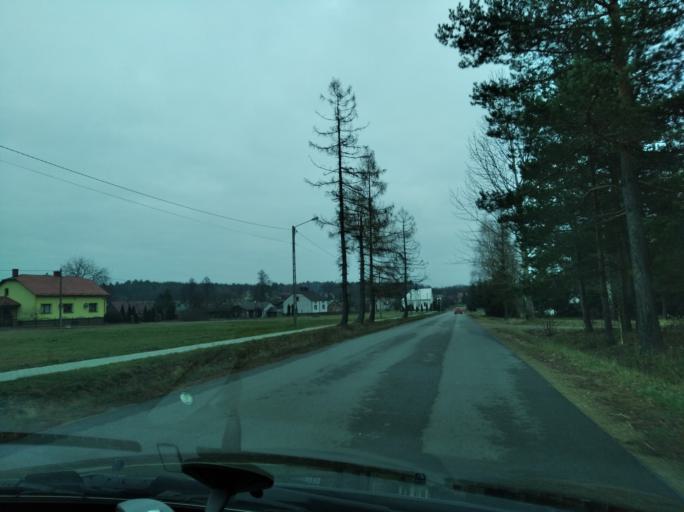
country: PL
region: Subcarpathian Voivodeship
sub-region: Powiat lancucki
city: Rakszawa
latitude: 50.1631
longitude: 22.1935
